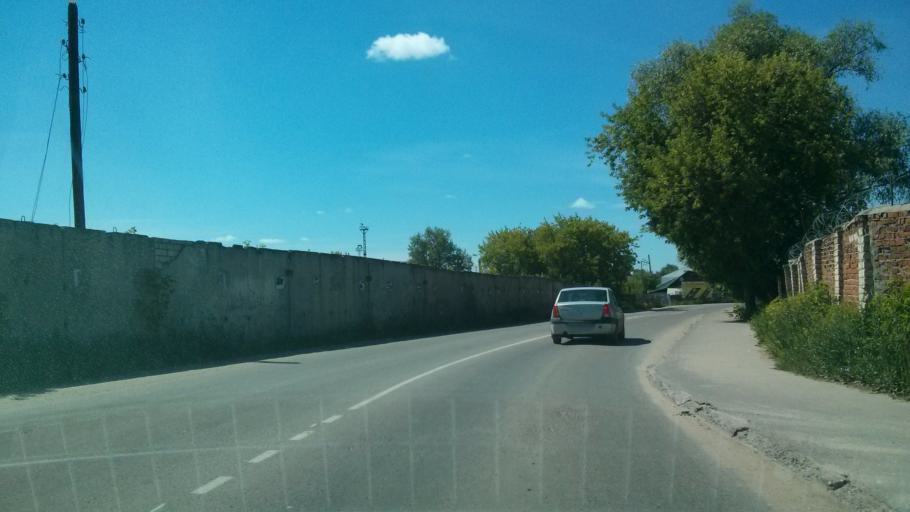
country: RU
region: Vladimir
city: Murom
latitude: 55.5632
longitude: 42.0328
